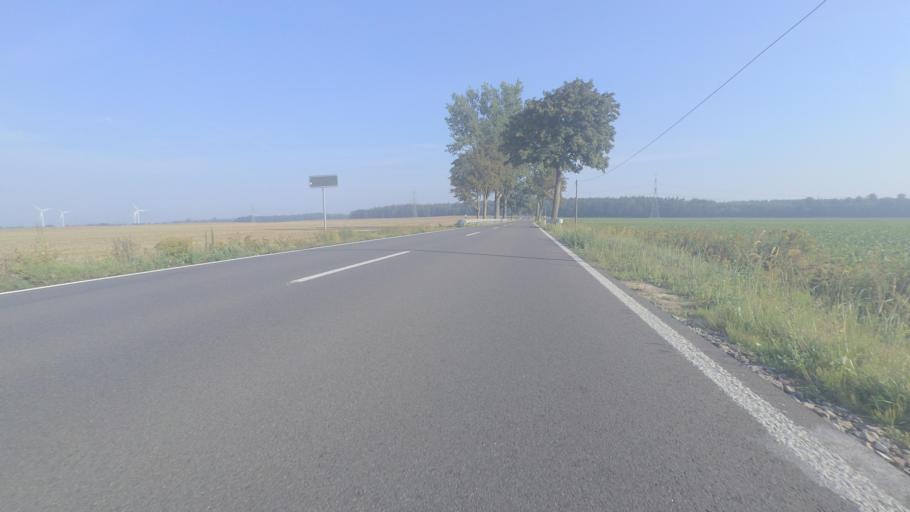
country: DE
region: Mecklenburg-Vorpommern
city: Gormin
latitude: 54.0165
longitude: 13.1390
